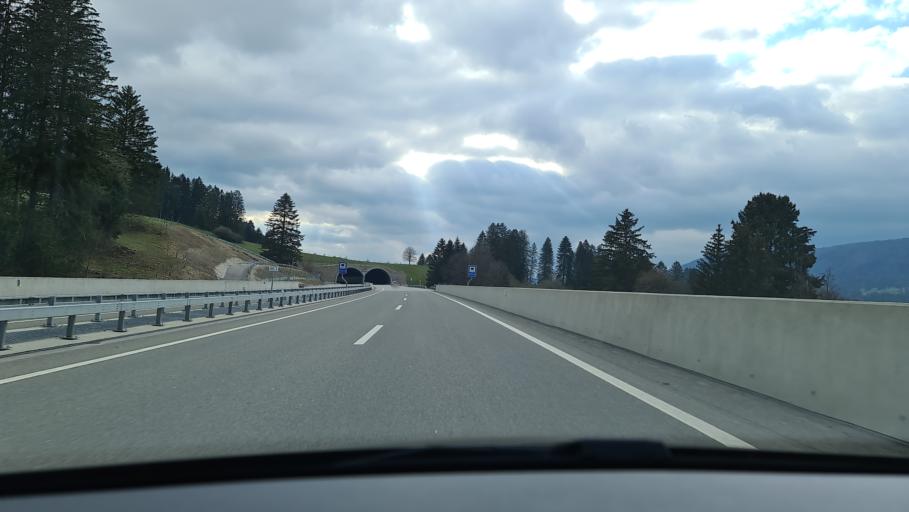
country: CH
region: Bern
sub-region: Jura bernois
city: Court
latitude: 47.2337
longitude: 7.3166
